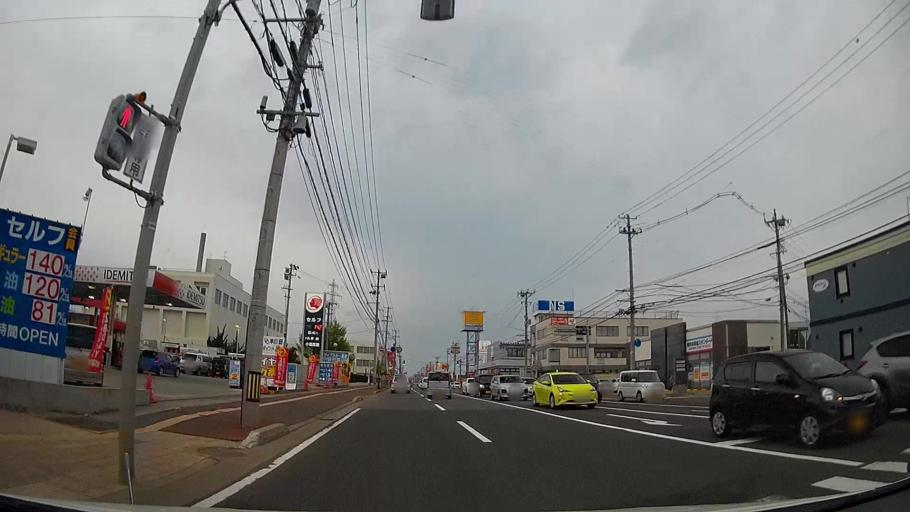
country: JP
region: Aomori
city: Aomori Shi
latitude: 40.8000
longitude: 140.7573
